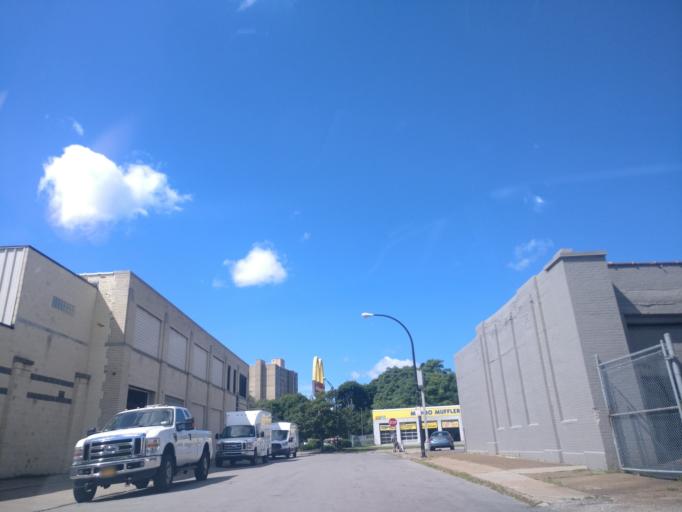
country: US
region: New York
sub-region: Erie County
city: Buffalo
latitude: 42.9103
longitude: -78.8654
